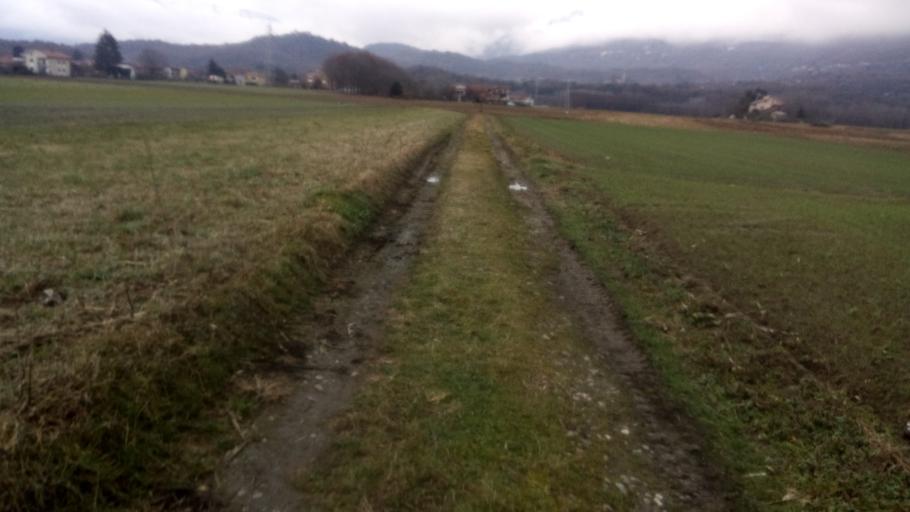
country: IT
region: Piedmont
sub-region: Provincia di Torino
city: Cascinette d'Ivrea
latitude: 45.4754
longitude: 7.9151
